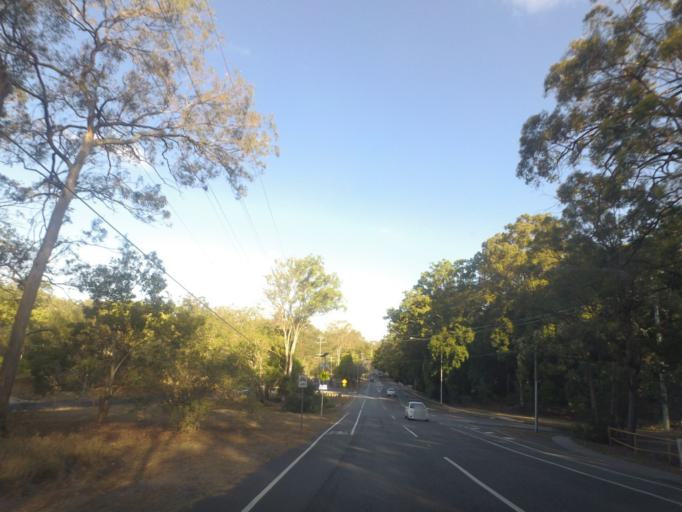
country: AU
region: Queensland
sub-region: Brisbane
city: Toowong
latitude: -27.4740
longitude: 152.9759
